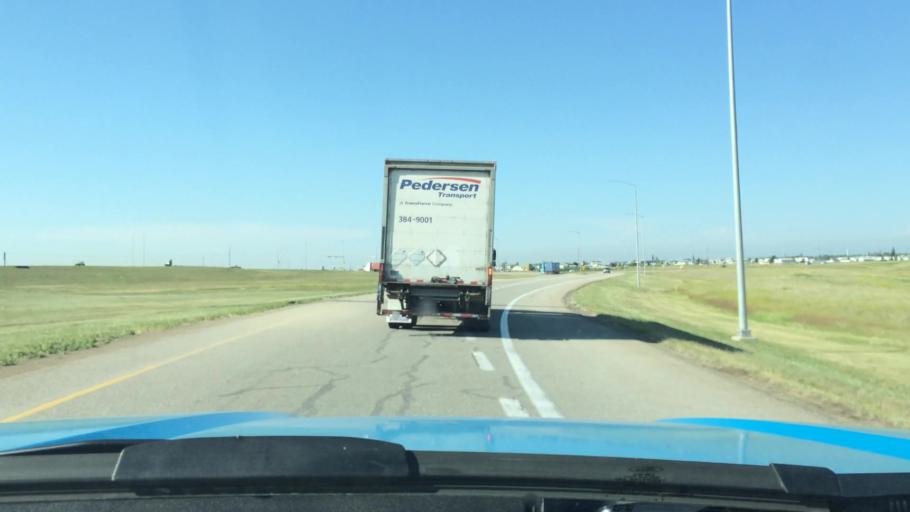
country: CA
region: Alberta
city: Chestermere
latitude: 51.1001
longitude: -113.9197
